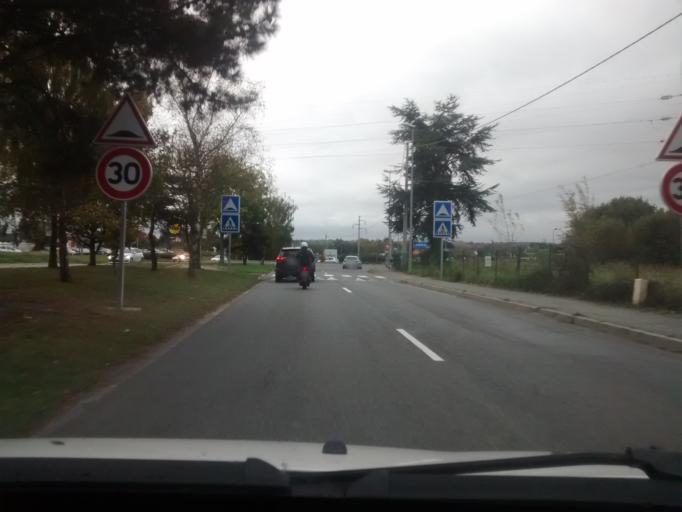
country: FR
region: Brittany
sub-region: Departement d'Ille-et-Vilaine
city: Dinard
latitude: 48.6160
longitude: -2.0579
